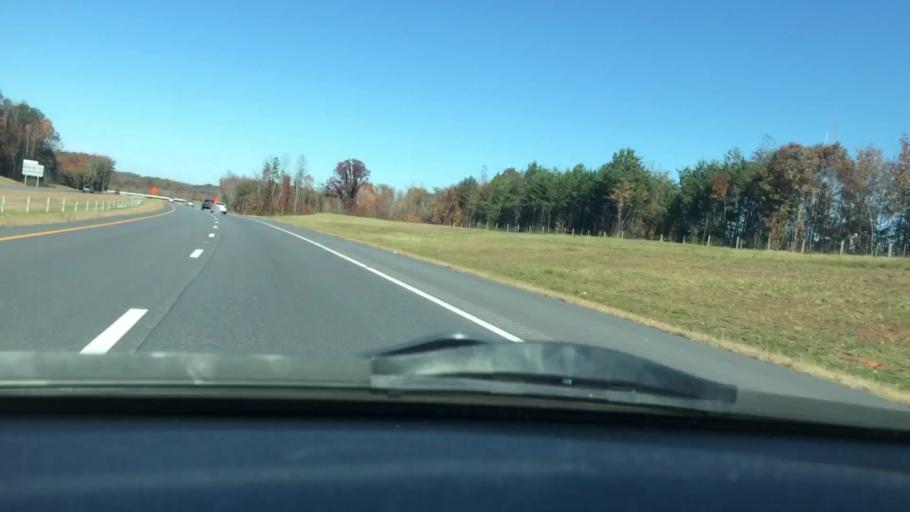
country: US
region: North Carolina
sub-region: Guilford County
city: Summerfield
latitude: 36.2171
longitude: -79.9164
